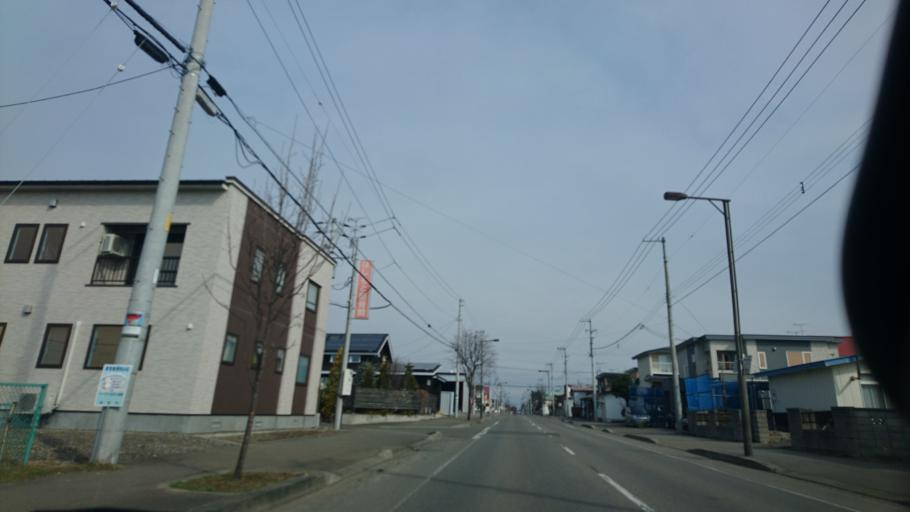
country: JP
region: Hokkaido
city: Otofuke
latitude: 42.9693
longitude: 143.2127
